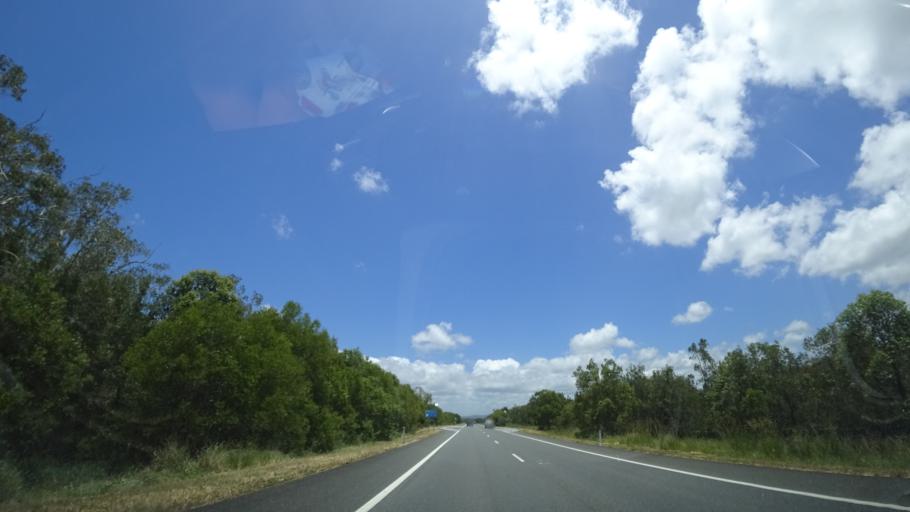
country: AU
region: Queensland
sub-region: Sunshine Coast
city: Little Mountain
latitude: -26.7669
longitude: 153.0938
